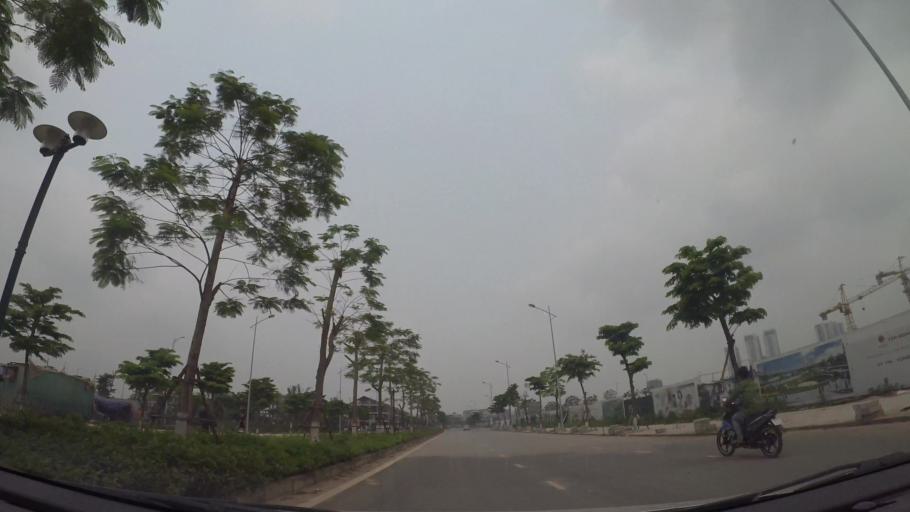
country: VN
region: Ha Noi
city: Ha Dong
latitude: 20.9826
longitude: 105.7575
